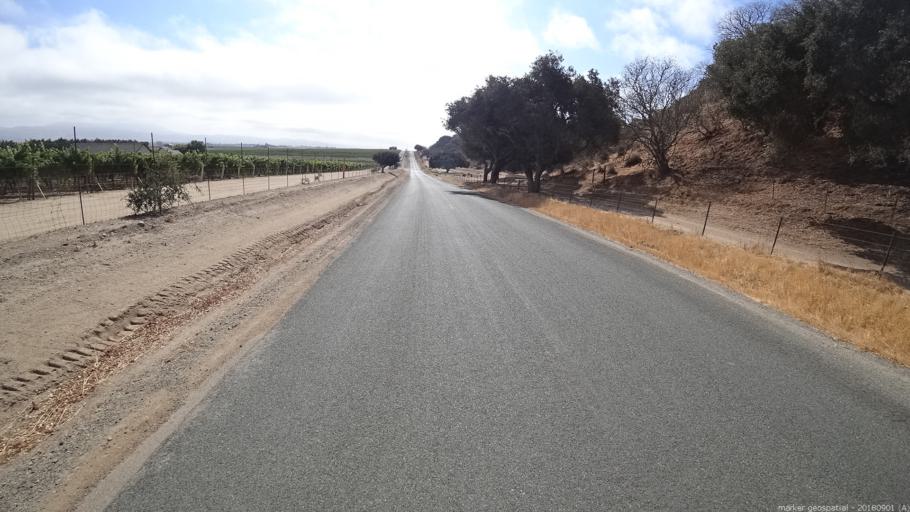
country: US
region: California
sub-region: Monterey County
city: Soledad
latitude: 36.4086
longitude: -121.3886
